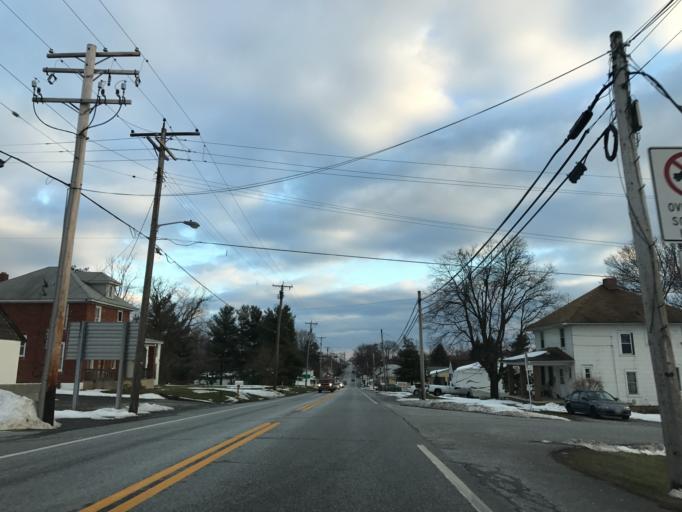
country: US
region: Pennsylvania
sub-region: York County
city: New Freedom
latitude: 39.7179
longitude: -76.6555
